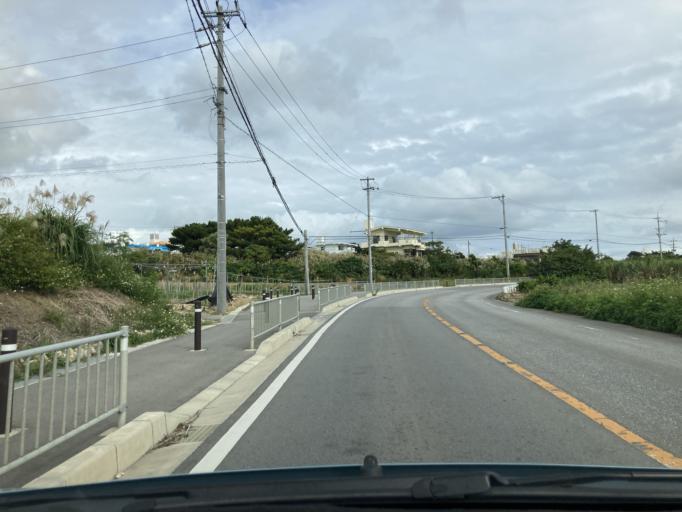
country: JP
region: Okinawa
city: Itoman
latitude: 26.1180
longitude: 127.6935
